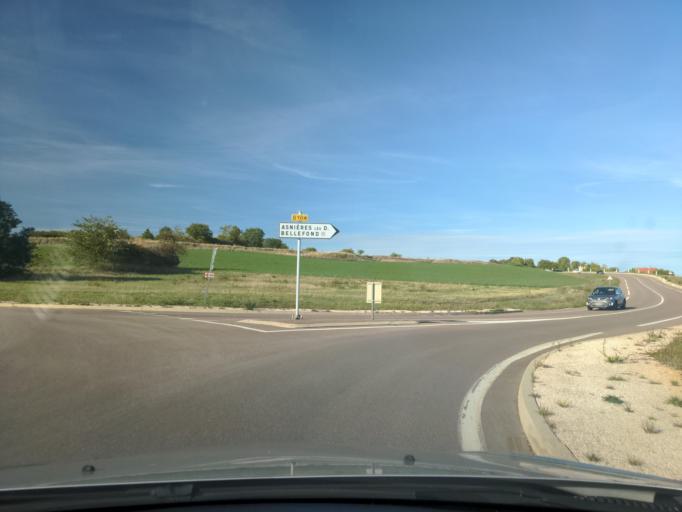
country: FR
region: Bourgogne
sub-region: Departement de la Cote-d'Or
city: Ruffey-les-Echirey
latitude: 47.3668
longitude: 5.0715
